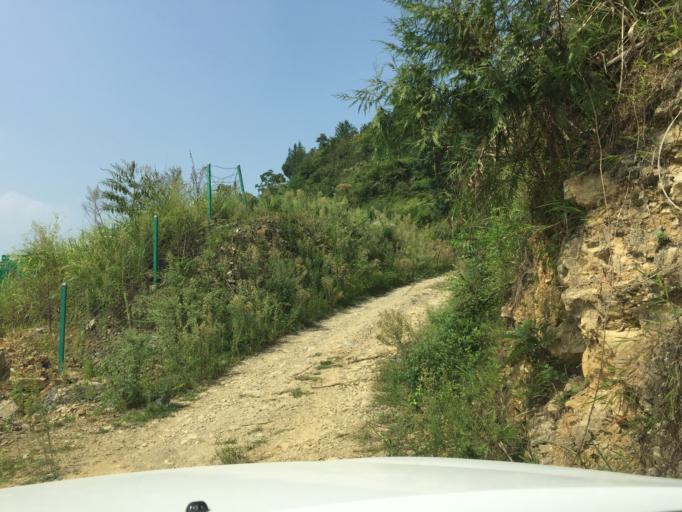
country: CN
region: Guizhou Sheng
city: Qinglong
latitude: 28.2939
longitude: 108.1106
